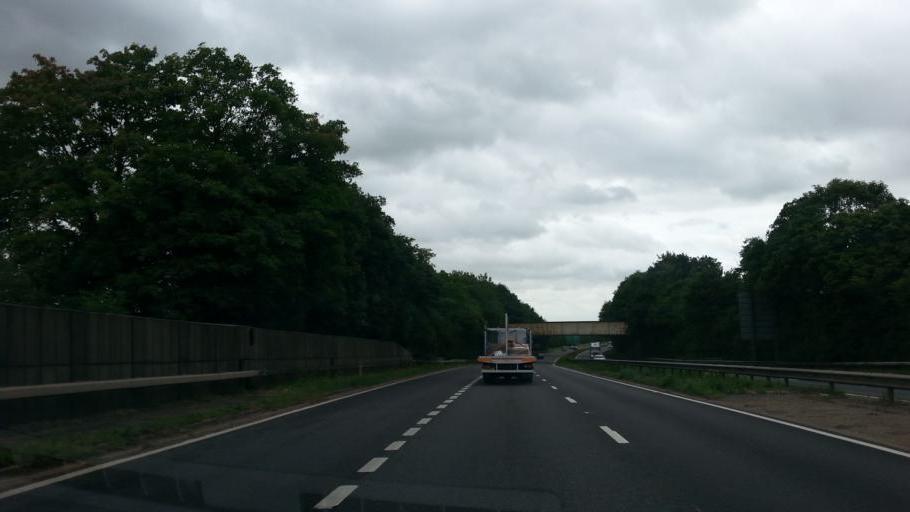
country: GB
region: England
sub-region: Warwickshire
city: Warwick
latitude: 52.2872
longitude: -1.6100
